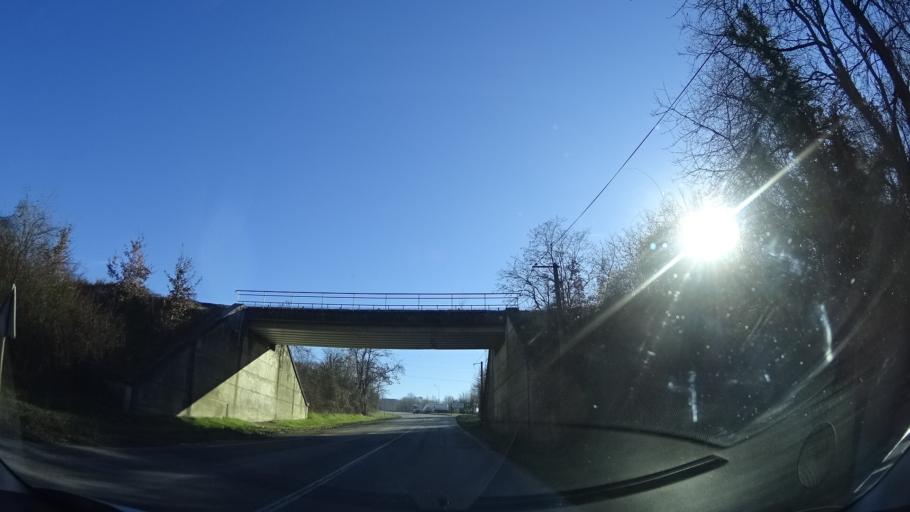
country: FR
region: Poitou-Charentes
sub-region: Departement des Deux-Sevres
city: Airvault
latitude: 46.8141
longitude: -0.1405
